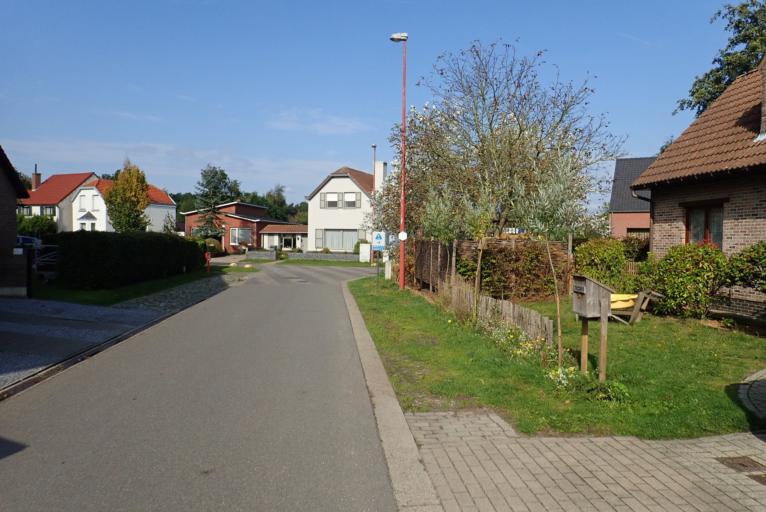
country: BE
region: Flanders
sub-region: Provincie Antwerpen
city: Kalmthout
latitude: 51.3999
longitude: 4.4646
